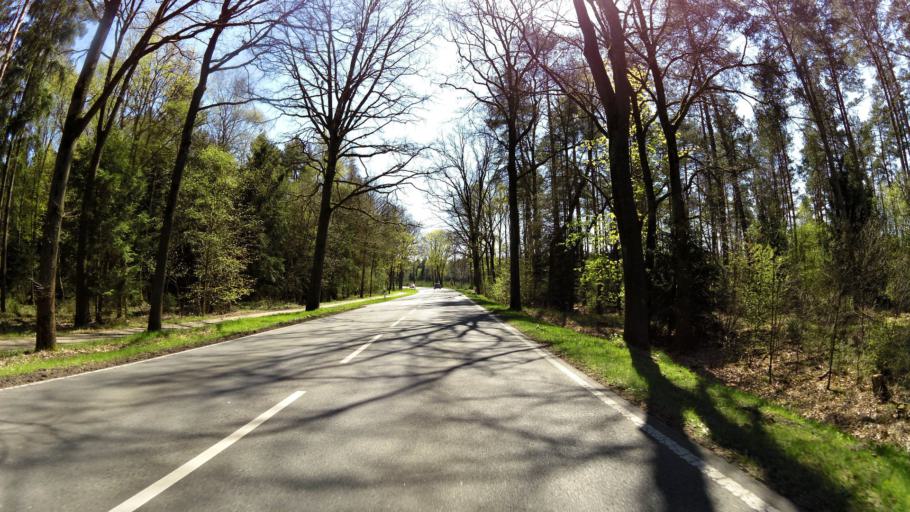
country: DE
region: Lower Saxony
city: Soltau
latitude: 53.0151
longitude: 9.7779
